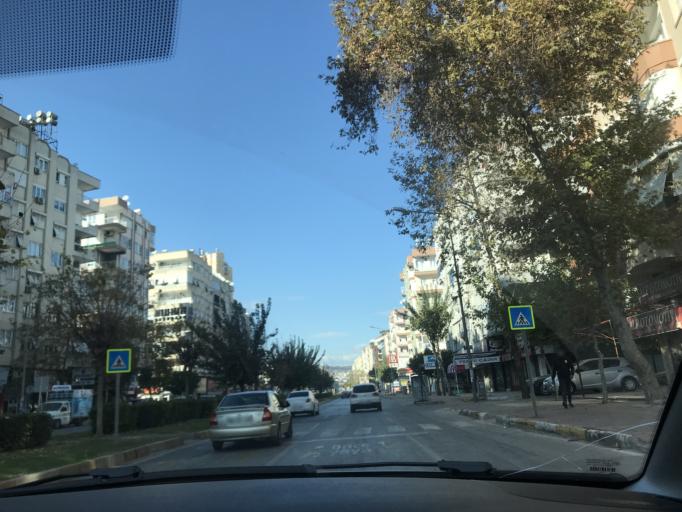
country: TR
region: Antalya
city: Antalya
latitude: 36.9052
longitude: 30.7004
